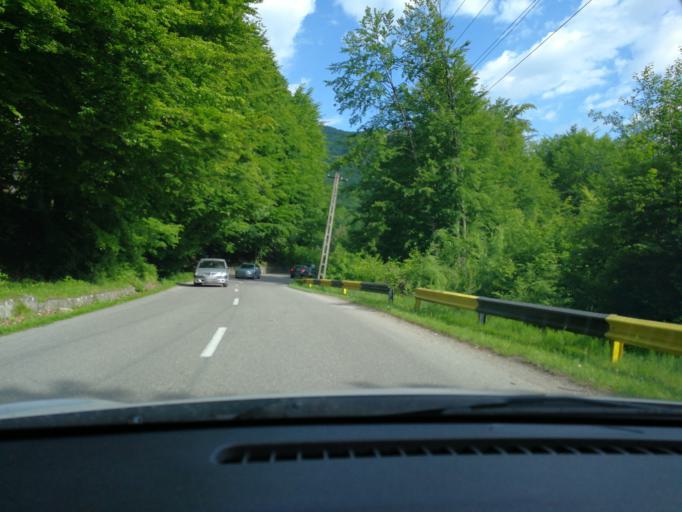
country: RO
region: Prahova
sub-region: Comuna Sotrile
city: Sotrile
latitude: 45.2563
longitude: 25.7389
